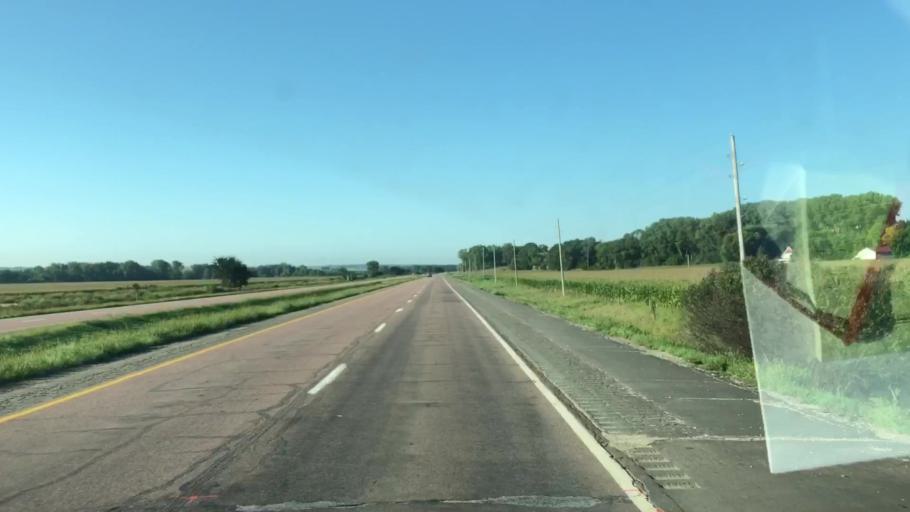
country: US
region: Iowa
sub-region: Woodbury County
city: Sioux City
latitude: 42.5933
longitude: -96.3056
